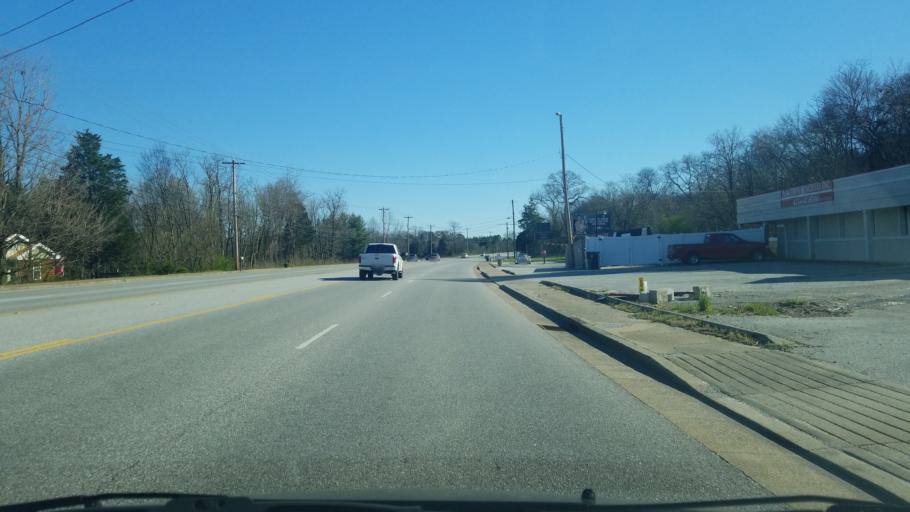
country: US
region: Tennessee
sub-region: Hamilton County
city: Middle Valley
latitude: 35.1634
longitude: -85.1906
